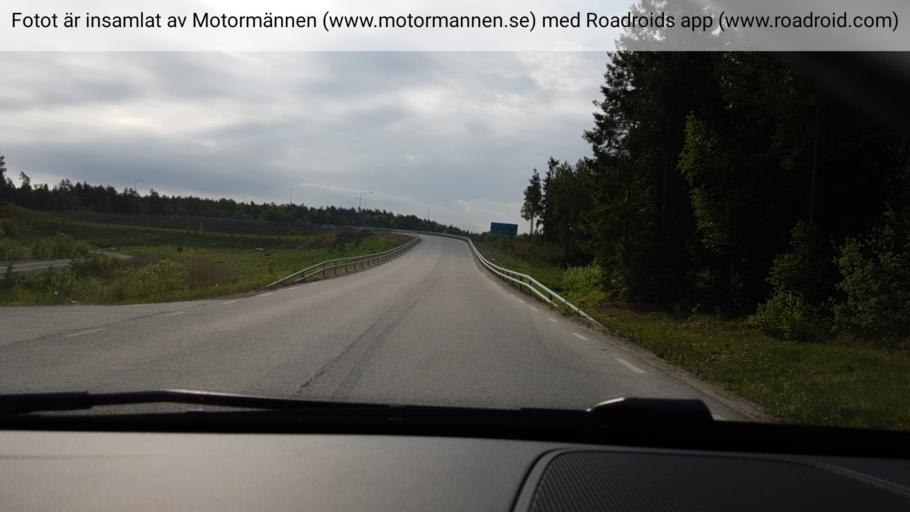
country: SE
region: Stockholm
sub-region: Nynashamns Kommun
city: Osmo
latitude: 59.0271
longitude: 17.9470
